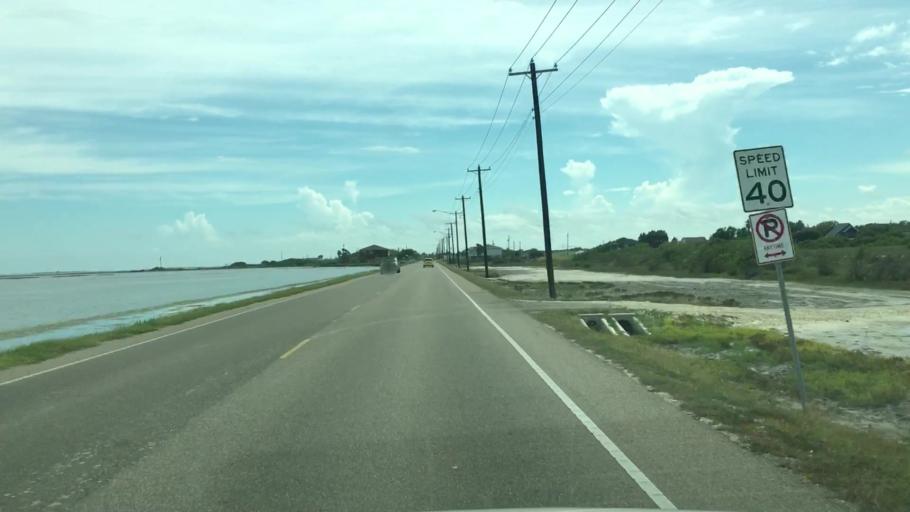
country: US
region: Texas
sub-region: Nueces County
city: Corpus Christi
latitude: 27.6506
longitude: -97.2803
